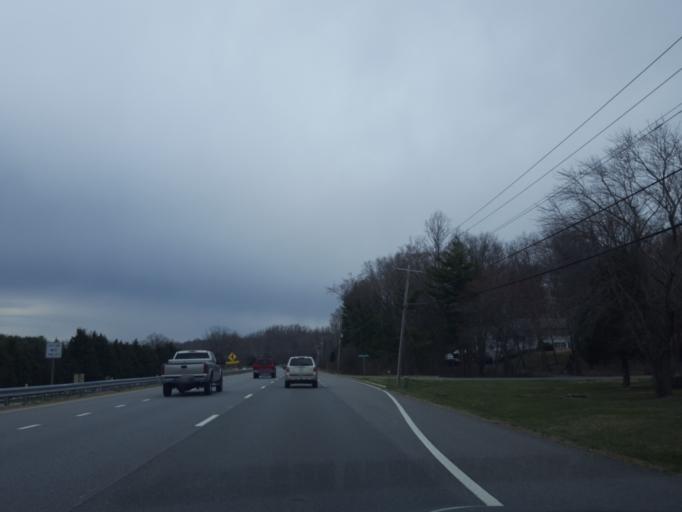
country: US
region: Maryland
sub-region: Calvert County
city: Dunkirk
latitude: 38.7434
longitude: -76.6610
